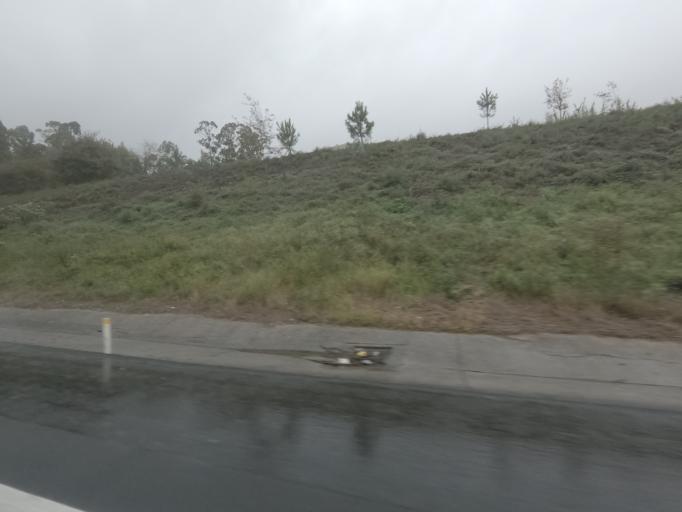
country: ES
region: Galicia
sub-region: Provincia de Pontevedra
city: Redondela
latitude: 42.2352
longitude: -8.6532
